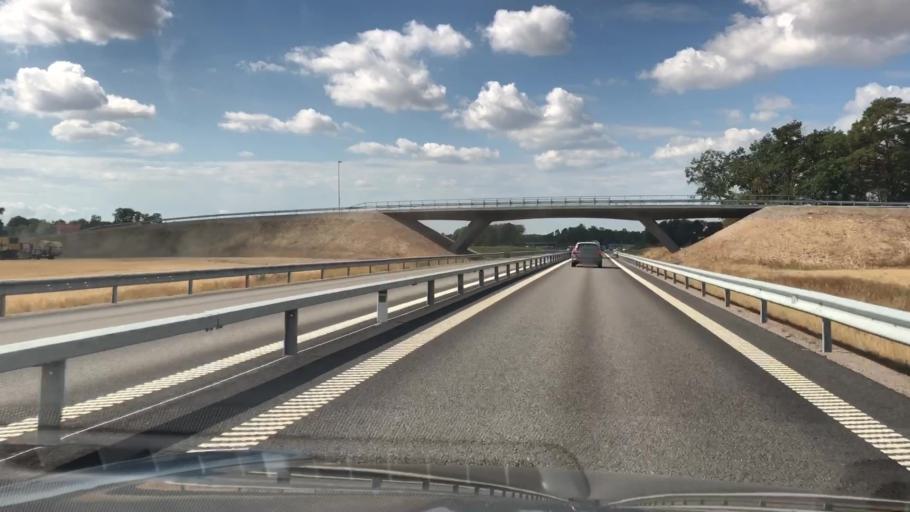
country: SE
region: Kalmar
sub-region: Kalmar Kommun
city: Rinkabyholm
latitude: 56.6428
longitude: 16.2259
